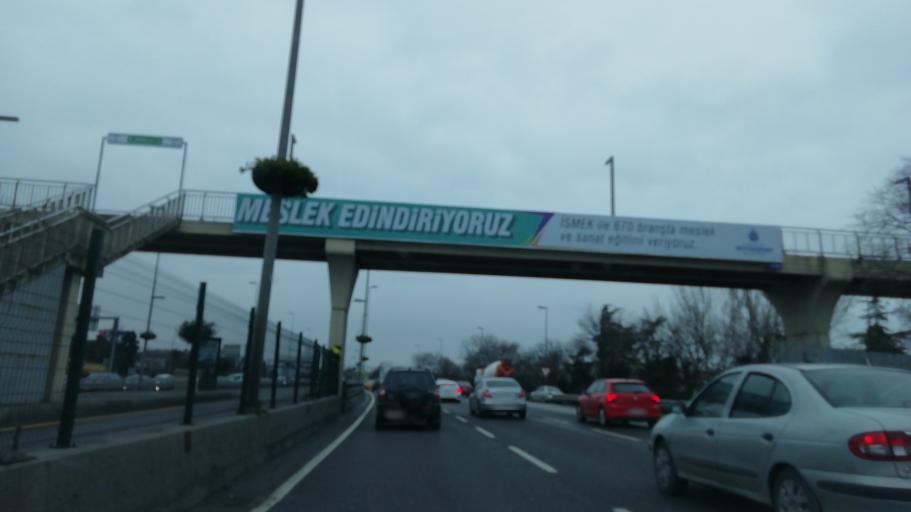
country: TR
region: Istanbul
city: UEskuedar
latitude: 41.0210
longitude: 29.0489
